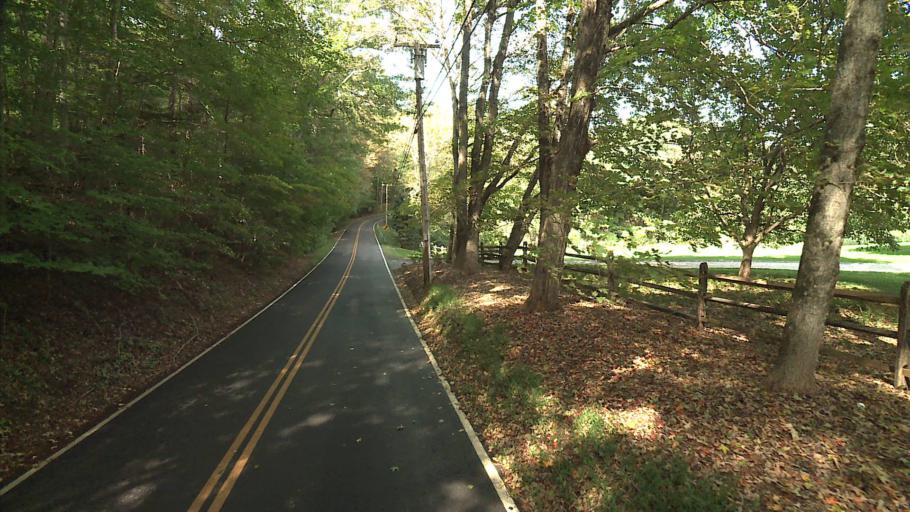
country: US
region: Connecticut
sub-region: Middlesex County
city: Chester Center
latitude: 41.4249
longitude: -72.4236
